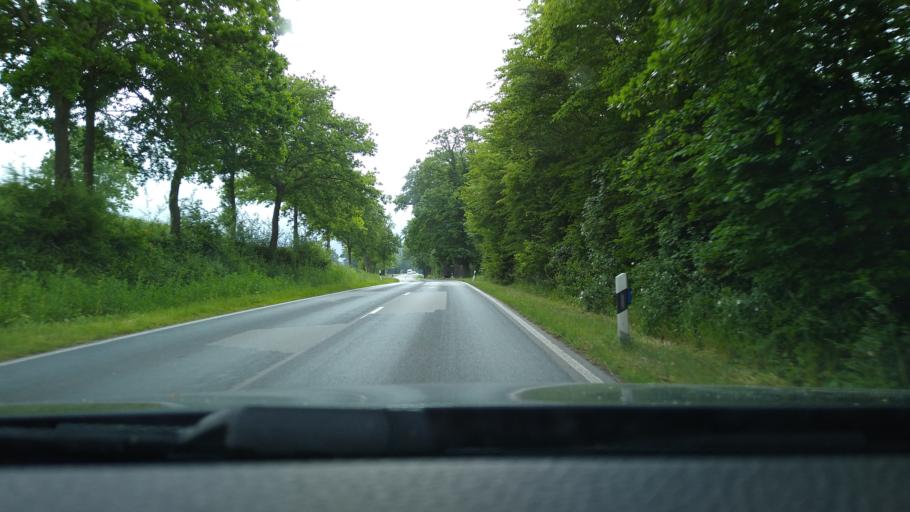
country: DE
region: Schleswig-Holstein
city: Kabelhorst
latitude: 54.2165
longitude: 10.9131
